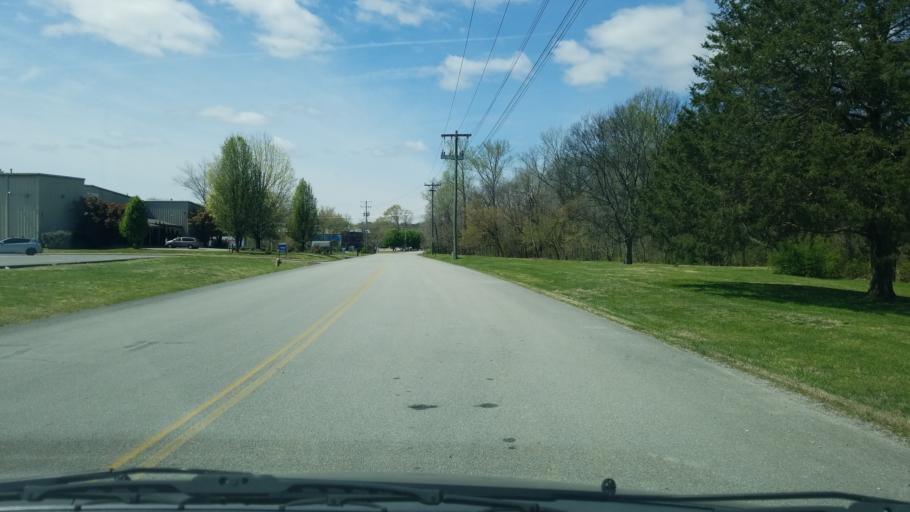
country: US
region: Tennessee
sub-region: Hamilton County
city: Collegedale
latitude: 35.0786
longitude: -85.0543
